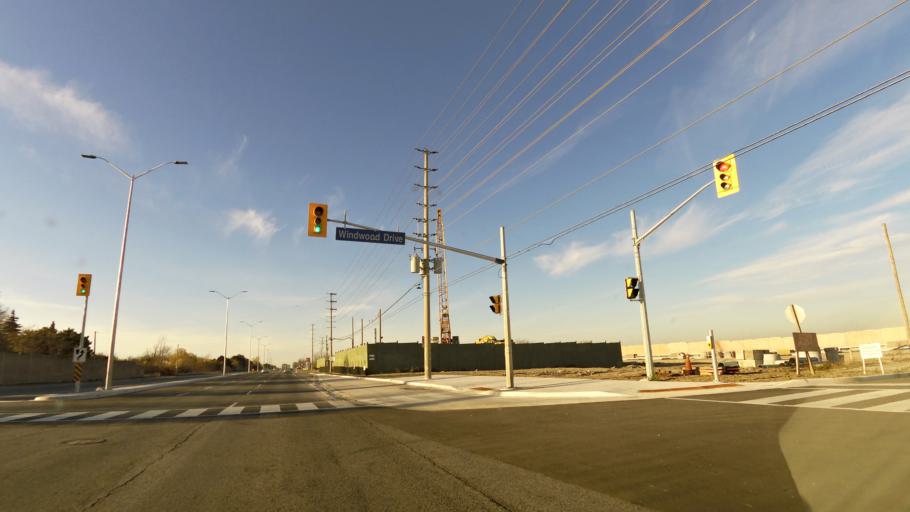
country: CA
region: Ontario
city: Mississauga
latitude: 43.5804
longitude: -79.7357
